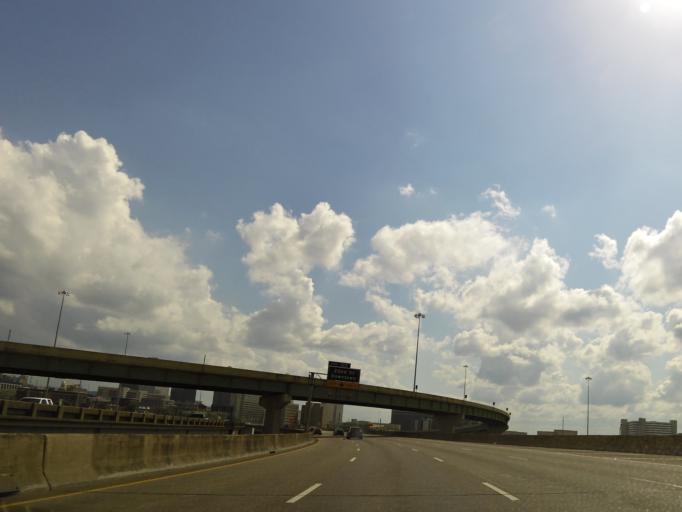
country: US
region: Alabama
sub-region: Jefferson County
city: Birmingham
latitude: 33.5288
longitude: -86.8032
